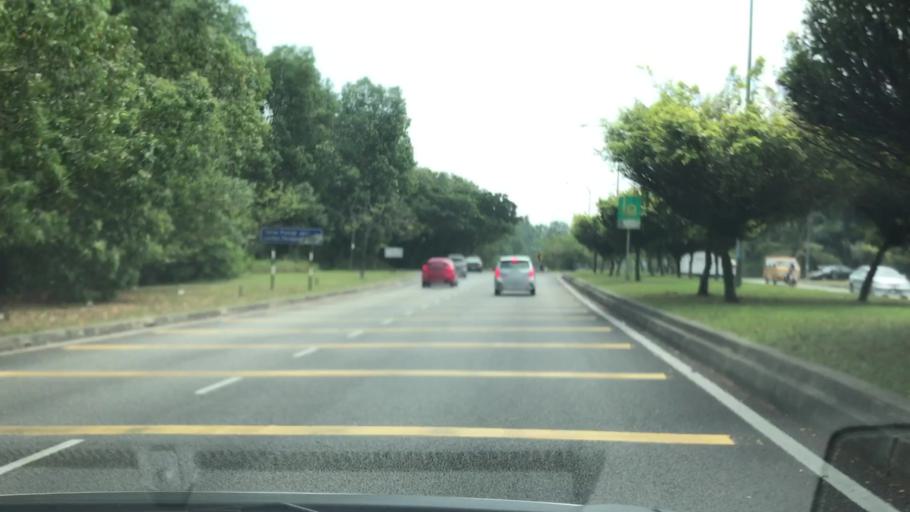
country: MY
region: Putrajaya
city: Putrajaya
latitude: 3.0043
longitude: 101.6655
